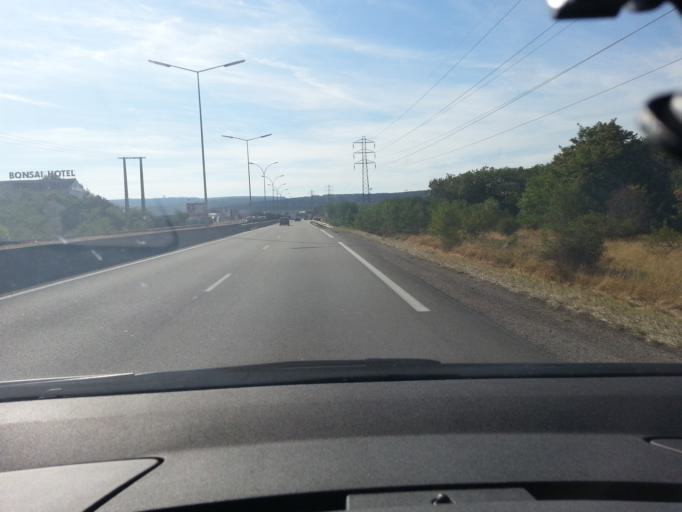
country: FR
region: Bourgogne
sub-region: Departement de la Cote-d'Or
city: Perrigny-les-Dijon
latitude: 47.2794
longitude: 5.0253
